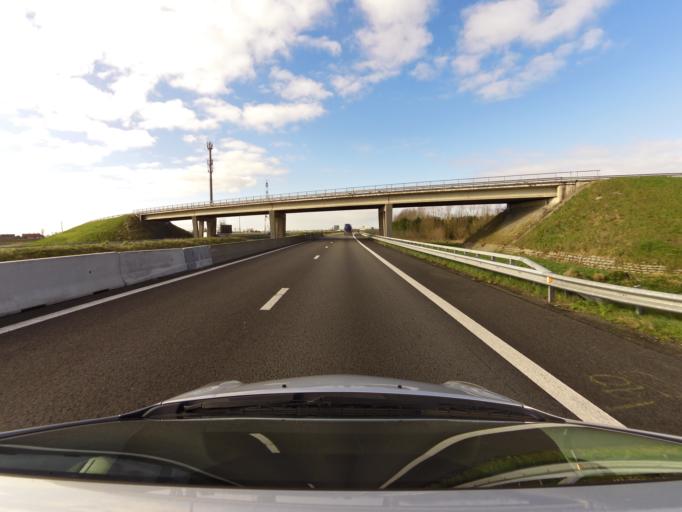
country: BE
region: Flanders
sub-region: Provincie West-Vlaanderen
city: Nieuwpoort
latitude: 51.0940
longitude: 2.7333
